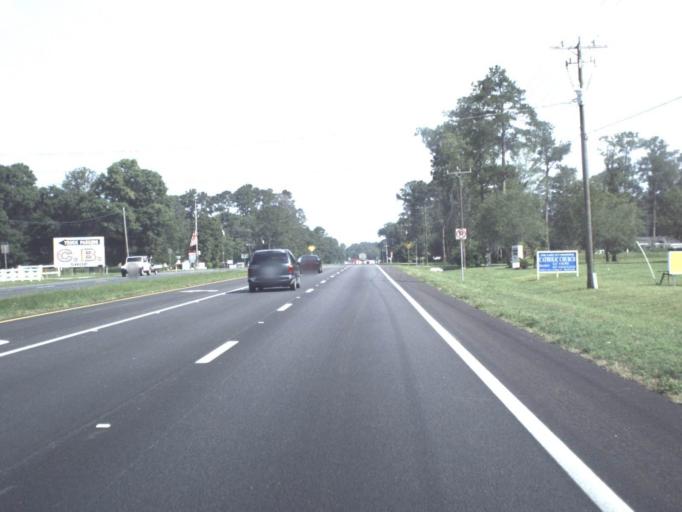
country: US
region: Florida
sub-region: Nassau County
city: Callahan
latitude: 30.5470
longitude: -81.8176
